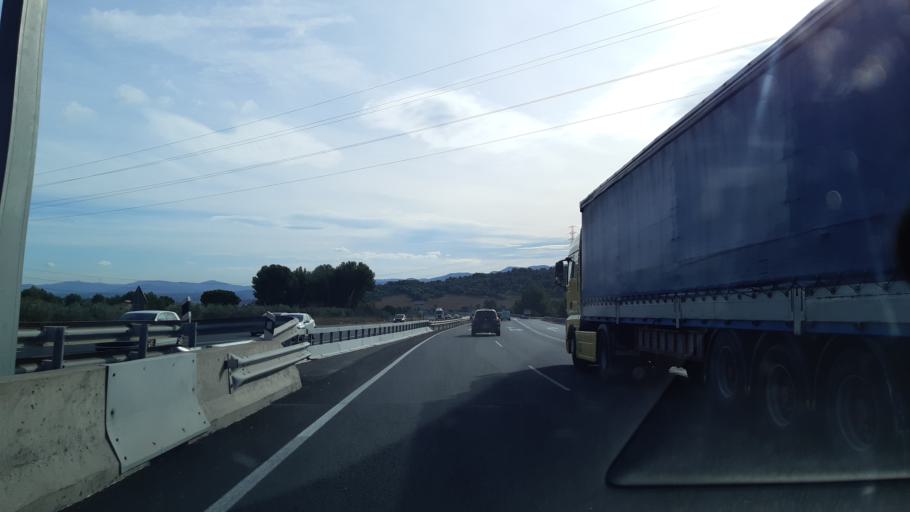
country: ES
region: Catalonia
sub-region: Provincia de Barcelona
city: Collbato
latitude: 41.5592
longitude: 1.8340
